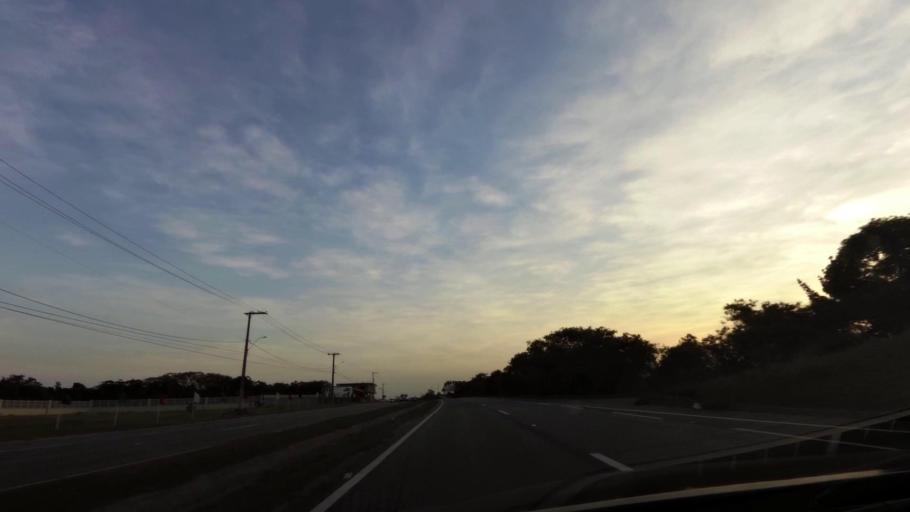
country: BR
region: Espirito Santo
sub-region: Guarapari
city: Guarapari
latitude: -20.5289
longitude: -40.3816
